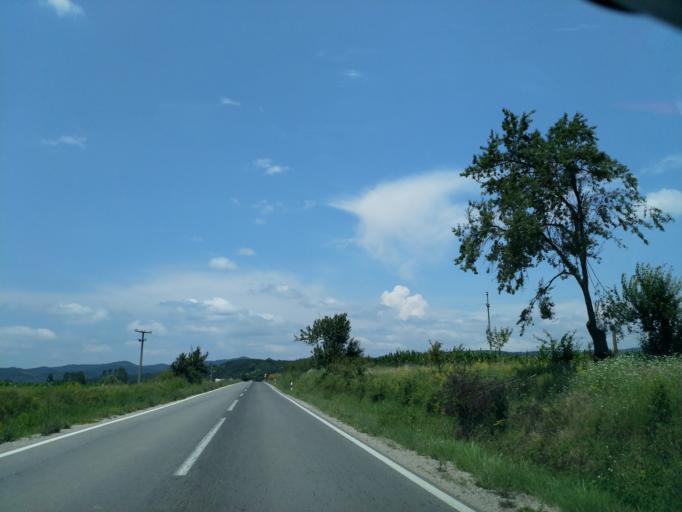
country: RS
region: Central Serbia
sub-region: Toplicki Okrug
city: Blace
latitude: 43.3081
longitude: 21.2480
